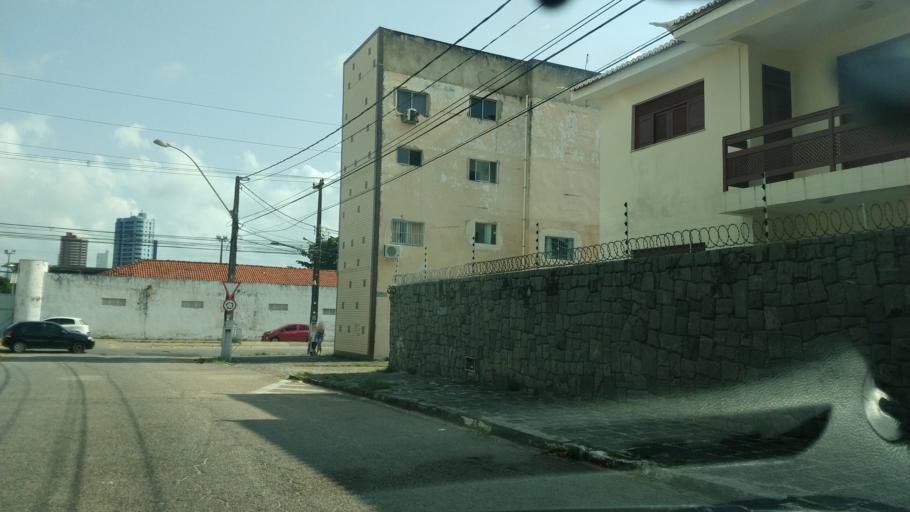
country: BR
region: Rio Grande do Norte
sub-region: Natal
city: Natal
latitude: -5.7939
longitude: -35.2022
